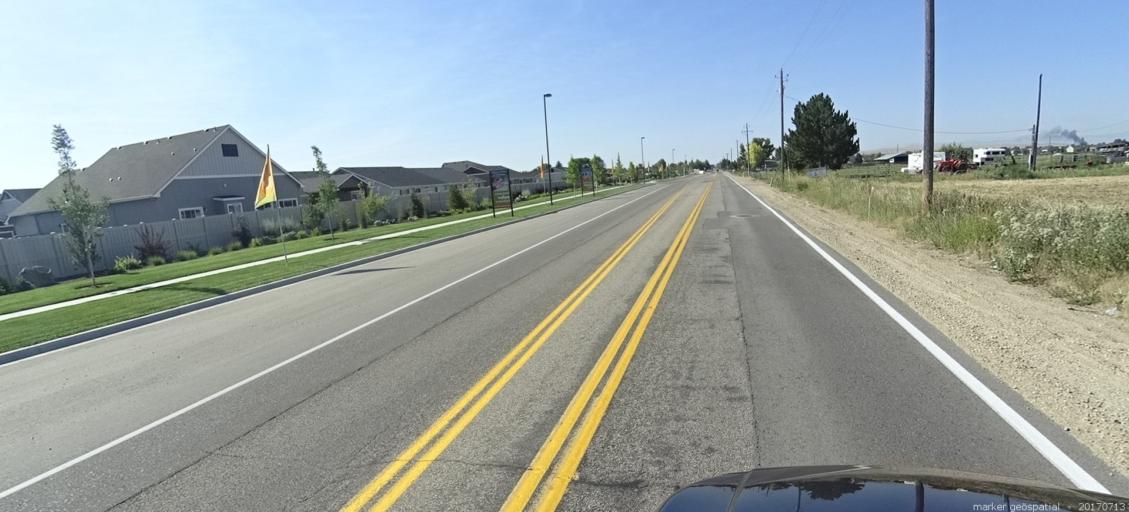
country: US
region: Idaho
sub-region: Ada County
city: Kuna
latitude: 43.5209
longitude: -116.4139
